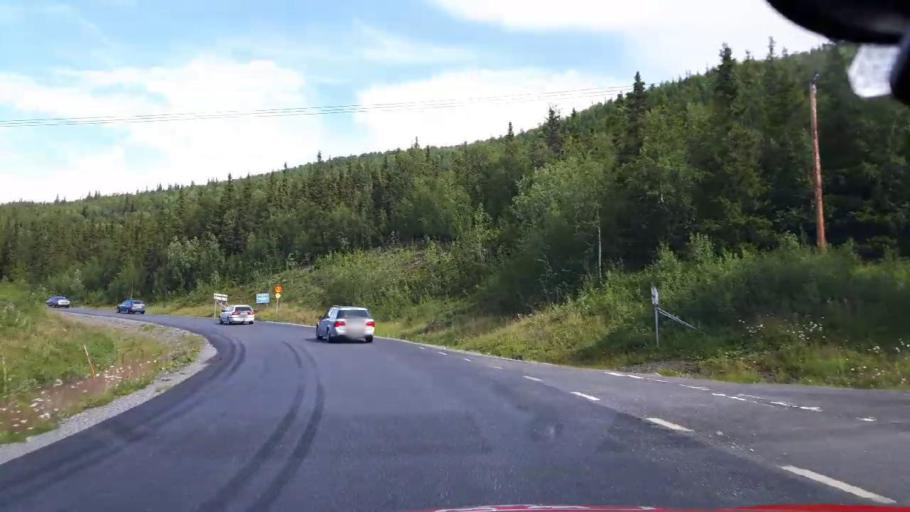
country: SE
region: Vaesterbotten
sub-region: Vilhelmina Kommun
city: Sjoberg
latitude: 65.0325
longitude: 15.1406
